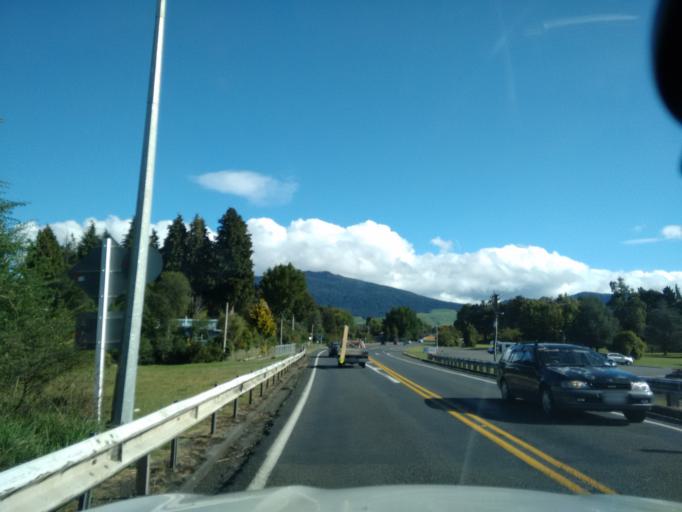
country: NZ
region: Waikato
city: Turangi
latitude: -38.9864
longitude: 175.8186
